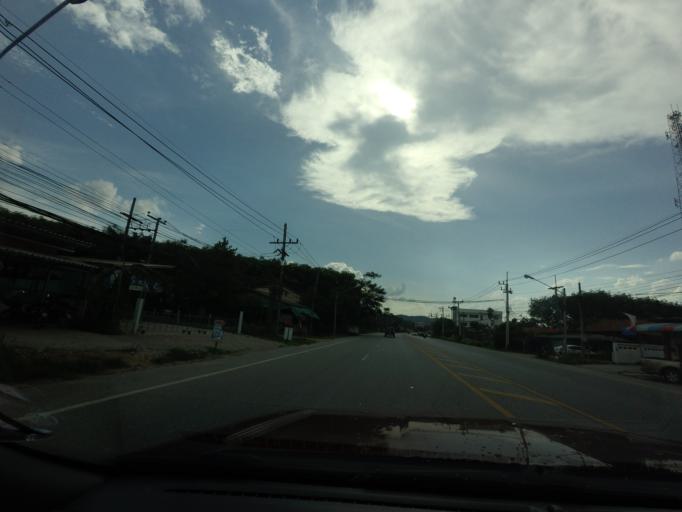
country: TH
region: Pattani
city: Khok Pho
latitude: 6.6757
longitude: 101.1498
